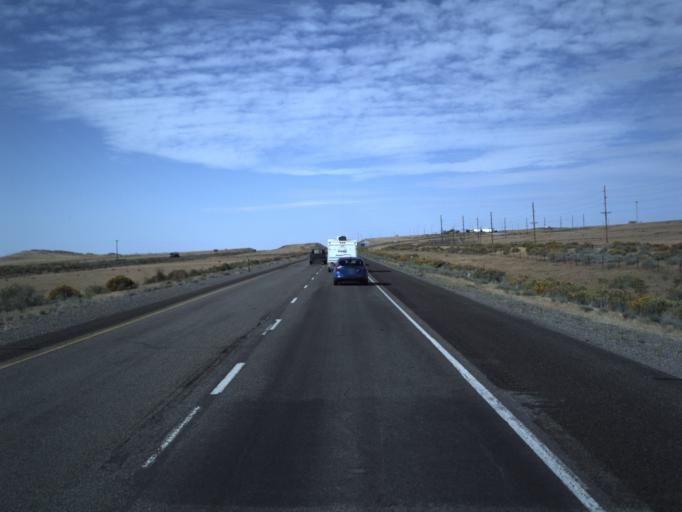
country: US
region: Utah
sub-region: Tooele County
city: Grantsville
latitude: 40.7646
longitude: -112.9967
